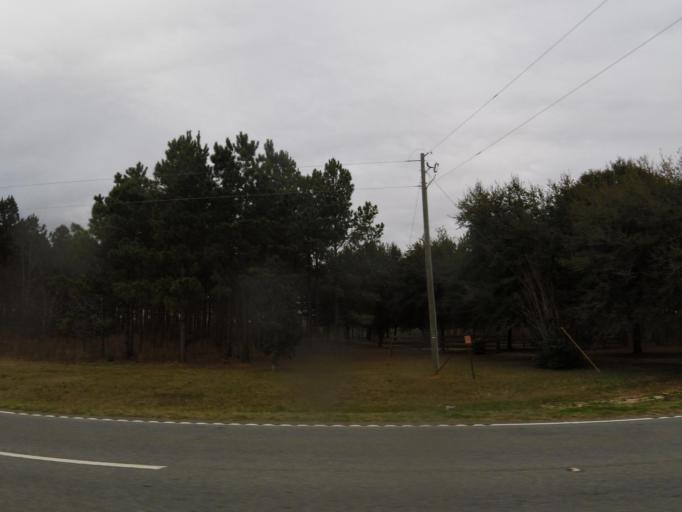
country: US
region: Georgia
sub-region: Randolph County
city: Shellman
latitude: 31.7813
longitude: -84.5880
